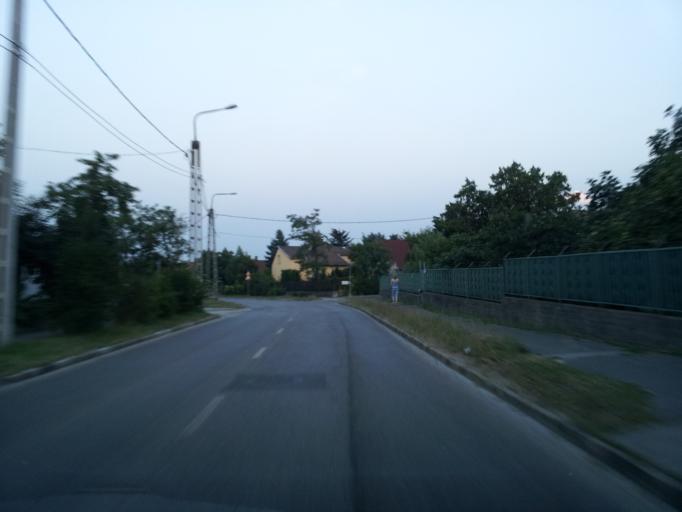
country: HU
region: Budapest
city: Budapest XXII. keruelet
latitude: 47.4236
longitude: 19.0261
